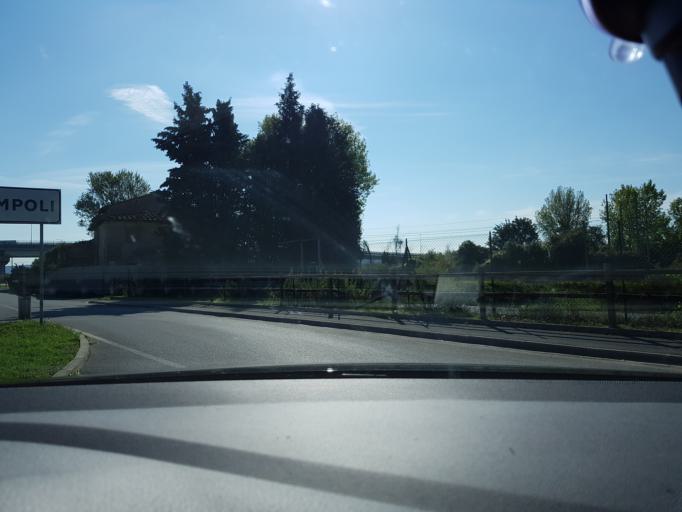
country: IT
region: Tuscany
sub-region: Province of Florence
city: Empoli
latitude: 43.7128
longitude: 10.9191
